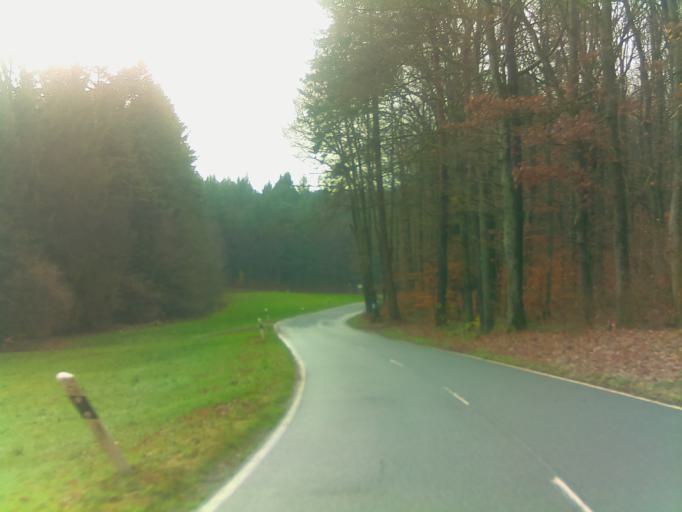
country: DE
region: Baden-Wuerttemberg
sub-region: Karlsruhe Region
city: Wilhelmsfeld
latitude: 49.4891
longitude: 8.7599
